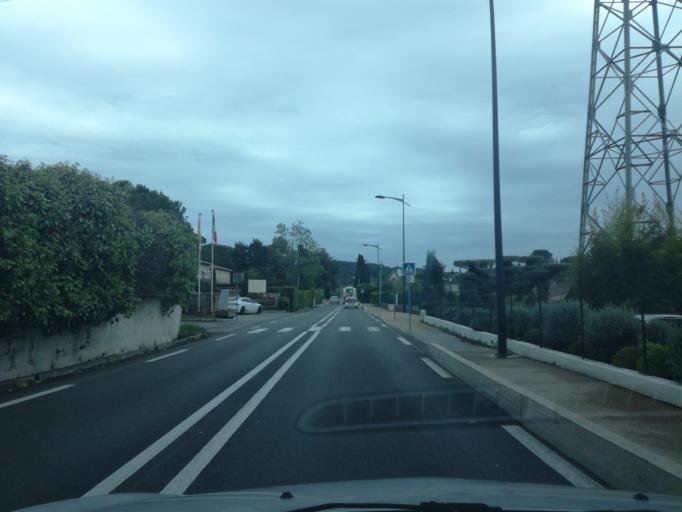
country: FR
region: Provence-Alpes-Cote d'Azur
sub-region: Departement des Alpes-Maritimes
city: Mougins
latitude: 43.6040
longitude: 7.0099
